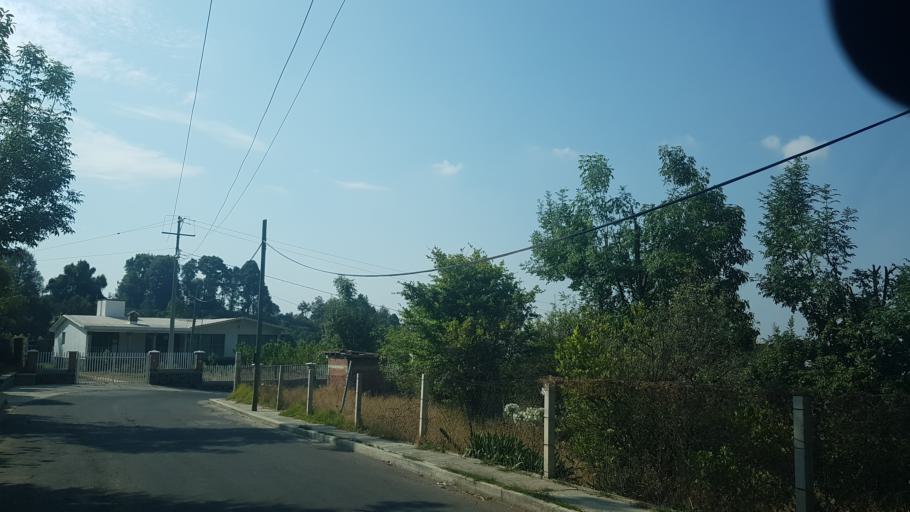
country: MX
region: Puebla
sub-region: Tochimilco
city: Santa Cruz Cuautomatitla
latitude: 18.8944
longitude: -98.6744
